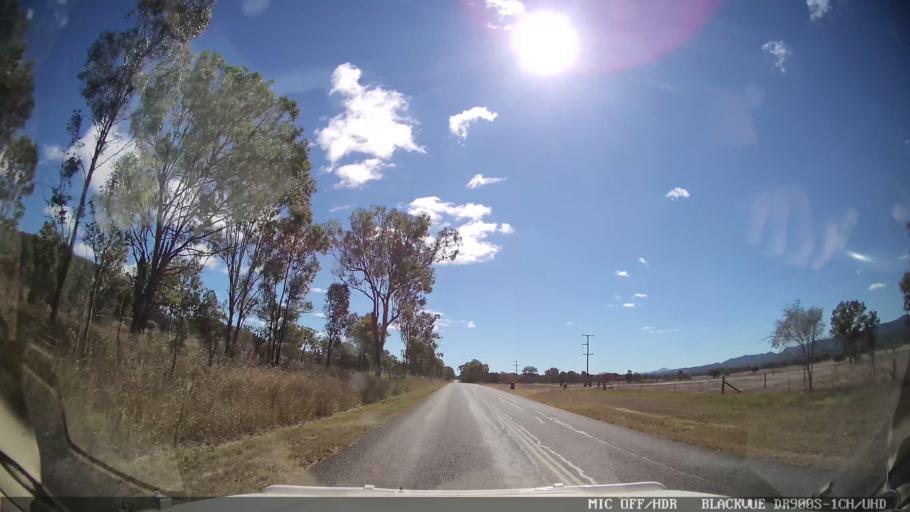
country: AU
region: Queensland
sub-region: Gladstone
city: Toolooa
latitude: -24.4507
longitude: 151.3453
